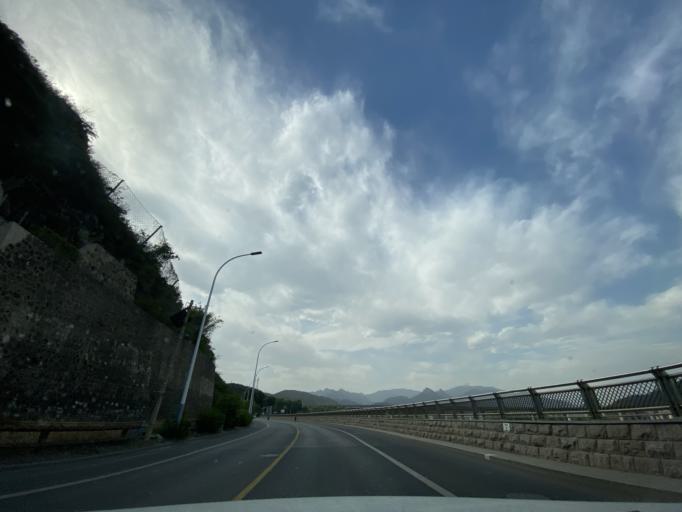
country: CN
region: Beijing
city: Chengzi
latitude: 39.9607
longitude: 116.0912
